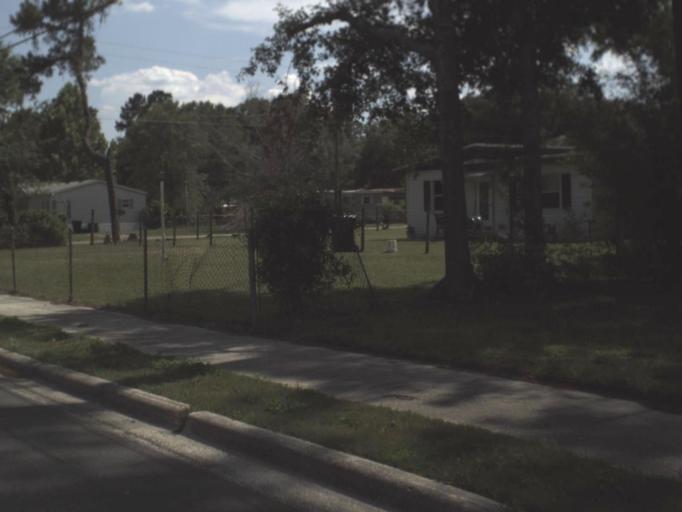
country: US
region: Florida
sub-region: Alachua County
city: Waldo
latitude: 29.7830
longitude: -82.1676
